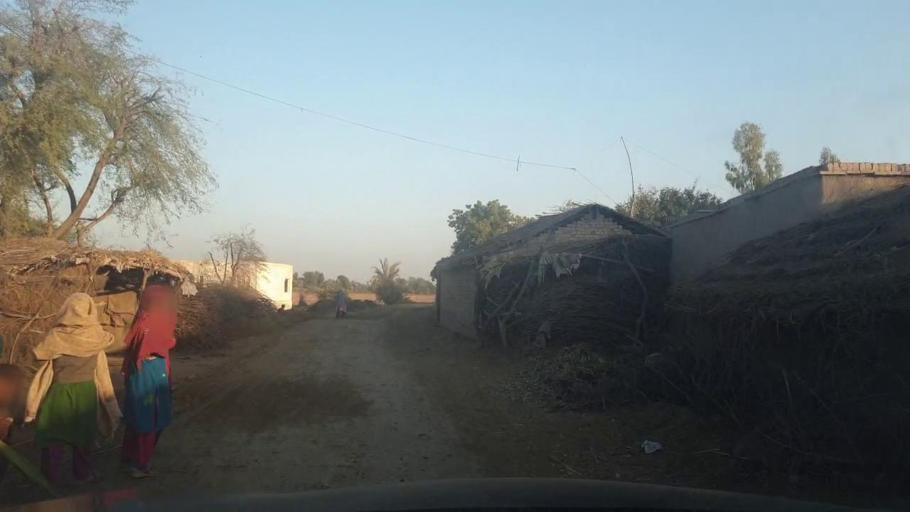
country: PK
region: Sindh
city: Mirpur Mathelo
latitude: 28.1738
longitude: 69.5734
